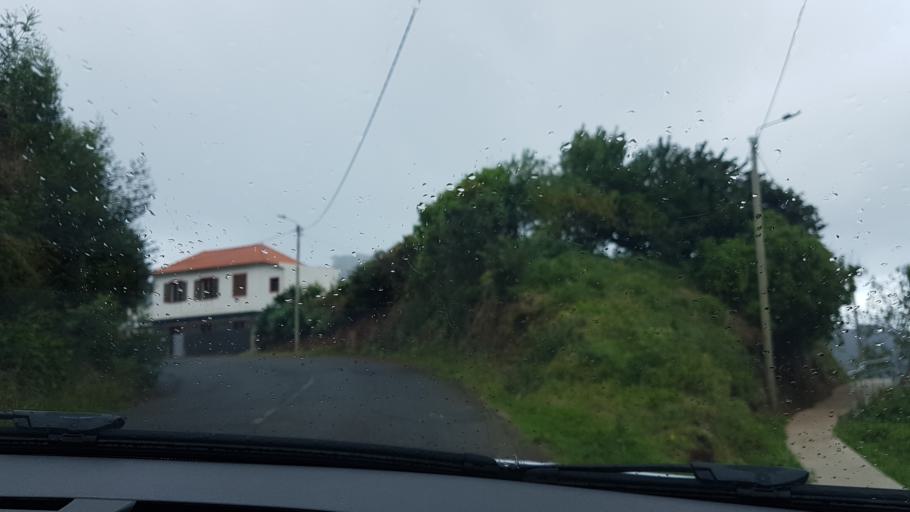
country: PT
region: Madeira
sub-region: Santa Cruz
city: Santa Cruz
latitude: 32.7313
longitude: -16.8111
